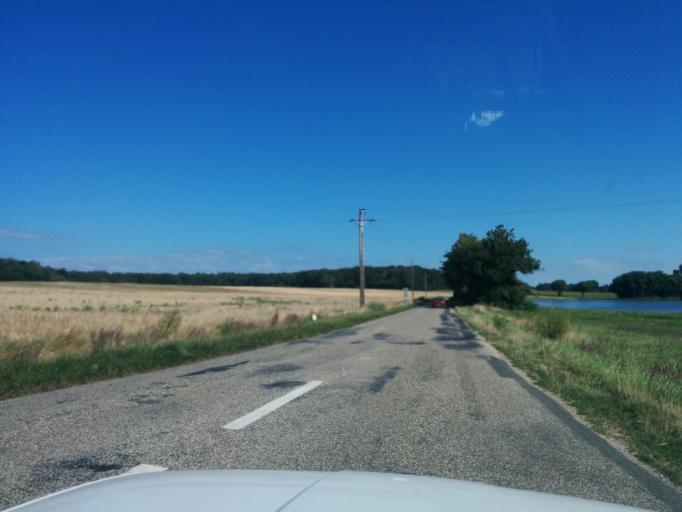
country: FR
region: Rhone-Alpes
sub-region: Departement de l'Ain
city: Chalamont
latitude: 45.9598
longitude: 5.1491
